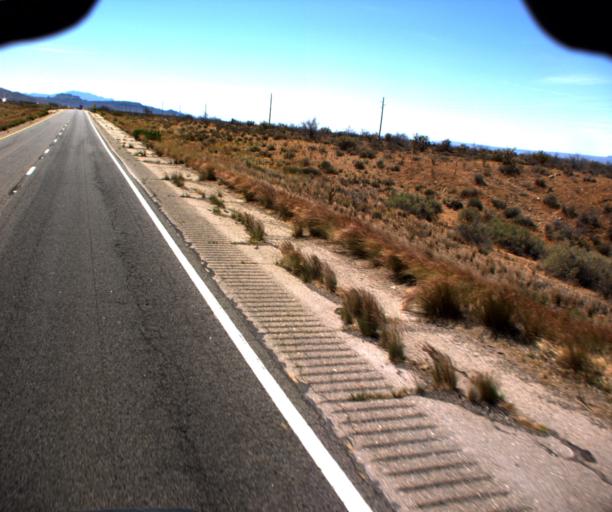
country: US
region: Arizona
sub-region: Mohave County
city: Golden Valley
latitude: 35.3056
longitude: -114.1935
